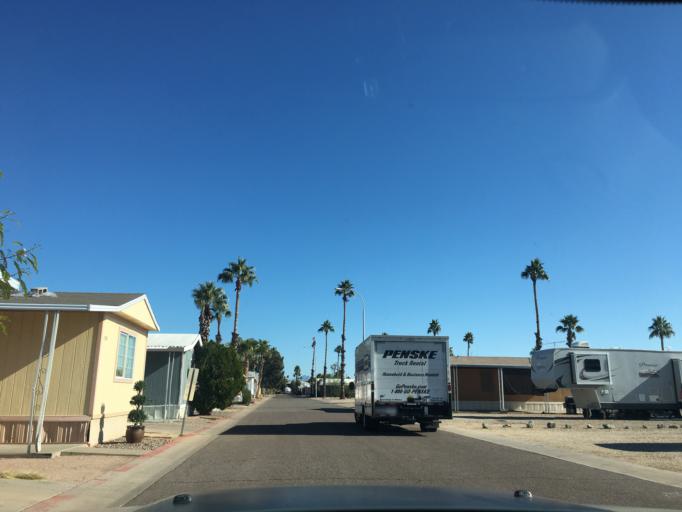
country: US
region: Arizona
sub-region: Maricopa County
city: Mesa
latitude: 33.4497
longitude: -111.8468
